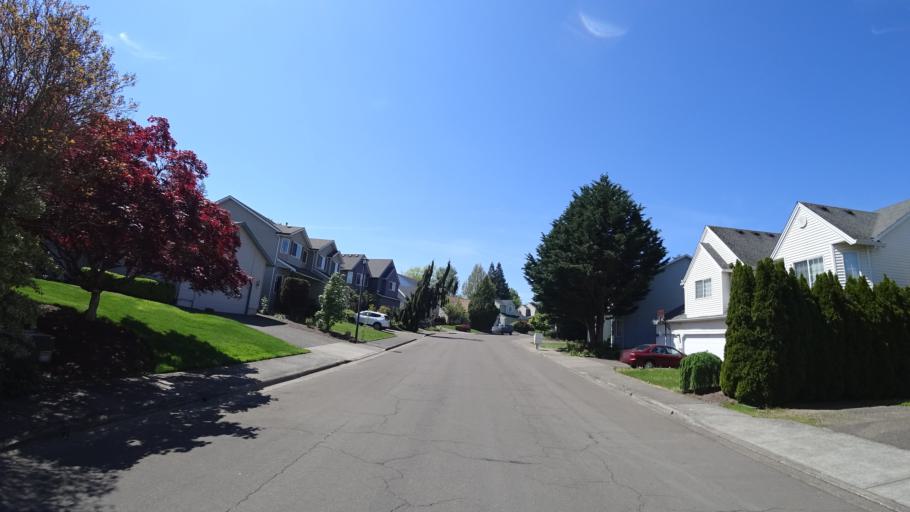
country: US
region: Oregon
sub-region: Washington County
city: King City
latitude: 45.4308
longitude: -122.8207
